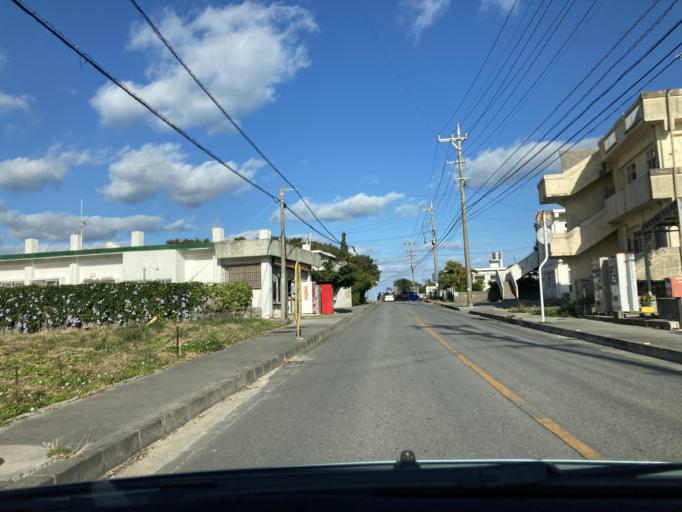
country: JP
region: Okinawa
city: Katsuren-haebaru
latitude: 26.3267
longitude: 127.8926
